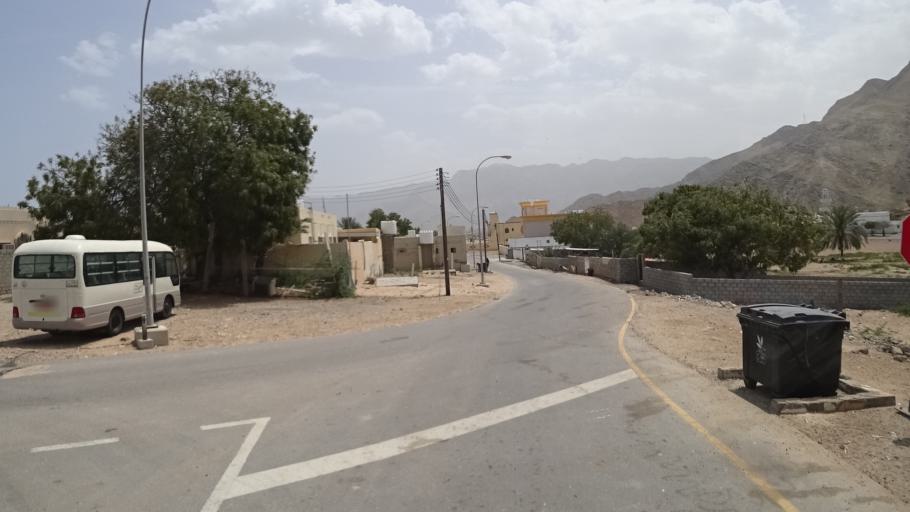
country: OM
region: Muhafazat Masqat
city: Muscat
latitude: 23.4373
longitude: 58.7805
